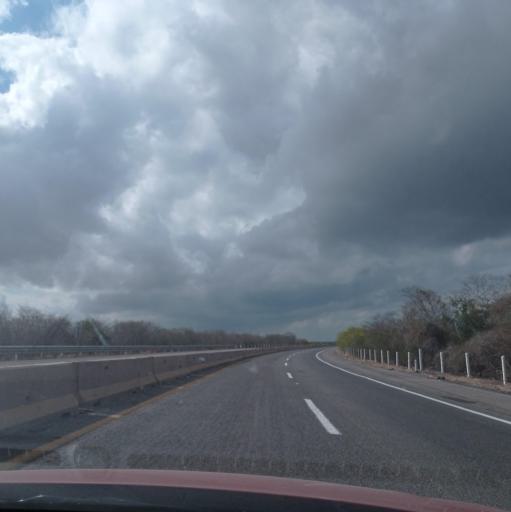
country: MX
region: Sinaloa
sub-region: Navolato
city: Juan Aldama (El Tigre)
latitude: 24.9906
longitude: -107.7726
